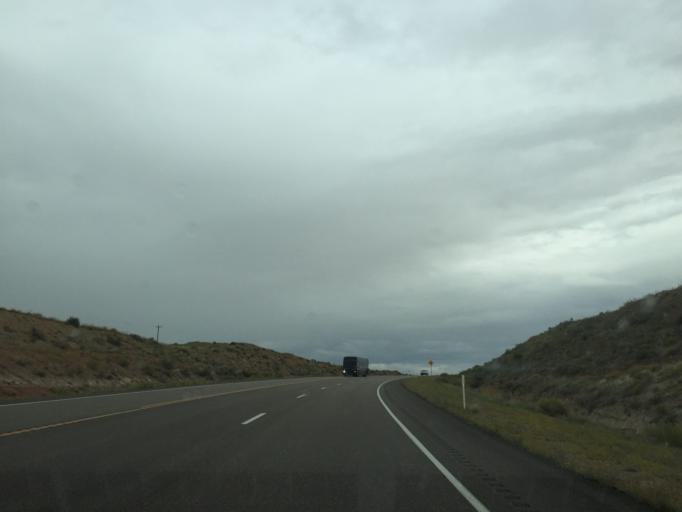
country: US
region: Arizona
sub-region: Coconino County
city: Page
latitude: 37.1038
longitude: -111.8603
